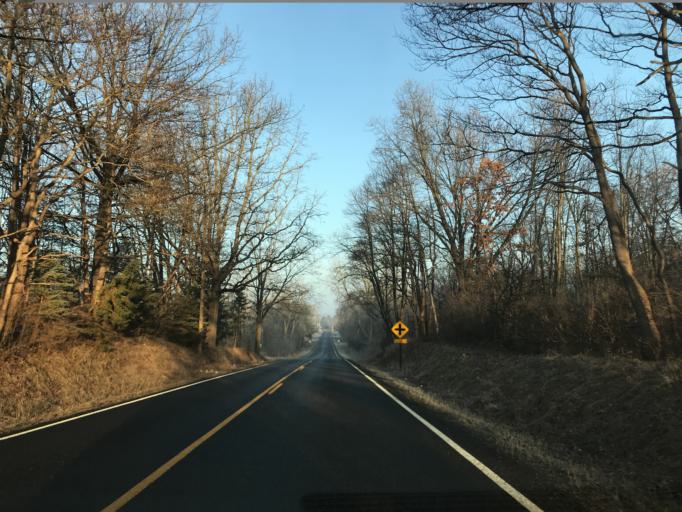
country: US
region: Michigan
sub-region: Ingham County
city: Leslie
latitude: 42.3907
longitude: -84.4596
